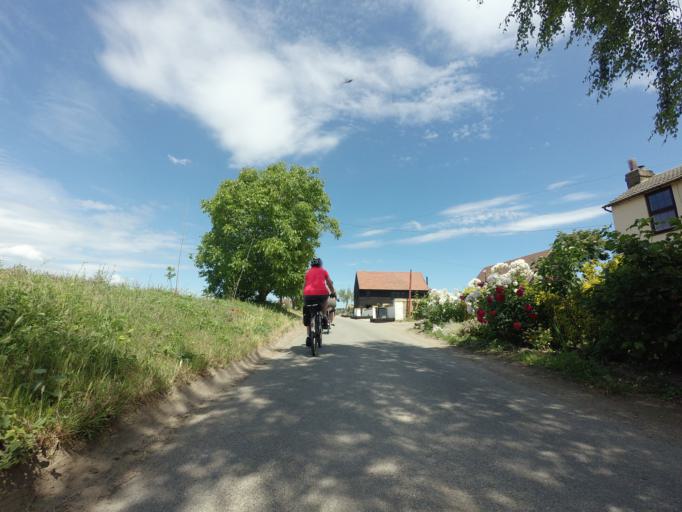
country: GB
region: England
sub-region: Kent
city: Cliffe
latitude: 51.4572
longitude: 0.4906
